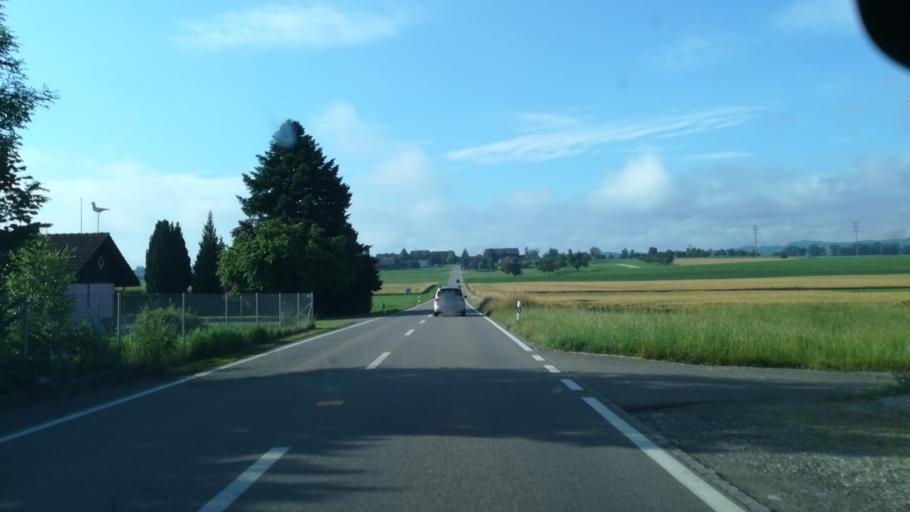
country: CH
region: Thurgau
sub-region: Weinfelden District
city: Sulgen
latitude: 47.5550
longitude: 9.1757
